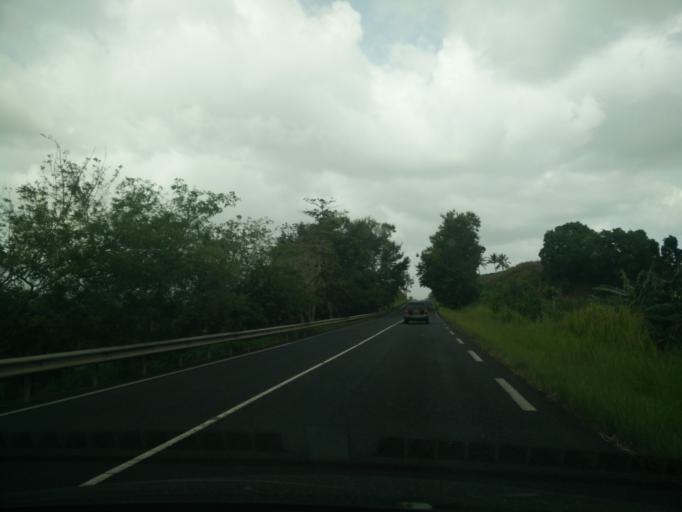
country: GP
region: Guadeloupe
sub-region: Guadeloupe
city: Petit-Bourg
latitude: 16.2163
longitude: -61.6156
